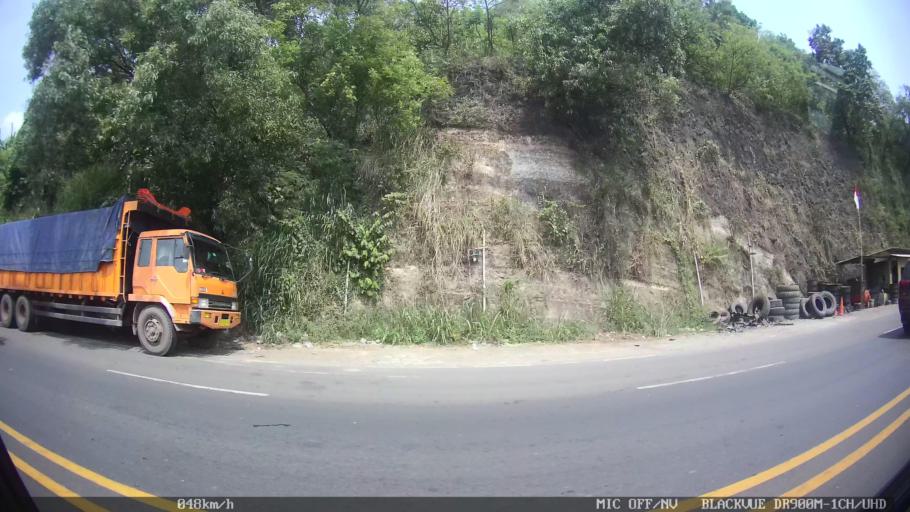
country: ID
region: Banten
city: Curug
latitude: -5.9489
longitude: 106.0028
